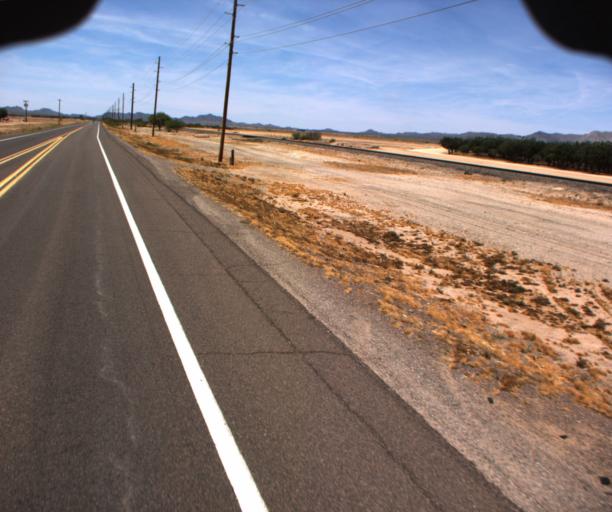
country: US
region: Arizona
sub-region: La Paz County
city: Salome
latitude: 33.8123
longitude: -113.5596
